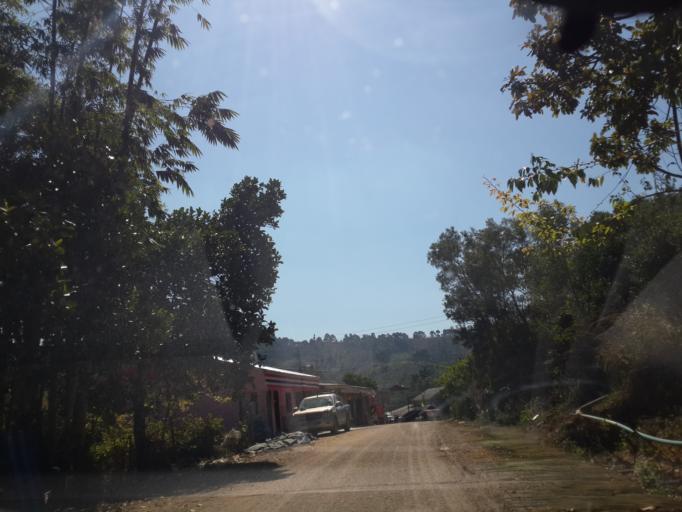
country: TH
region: Chiang Mai
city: Fang
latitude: 19.9395
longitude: 99.0420
